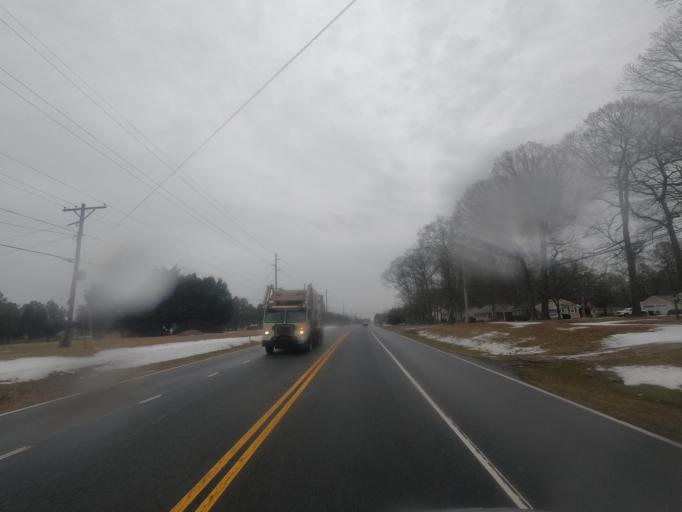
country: US
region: Maryland
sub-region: Dorchester County
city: Cambridge
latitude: 38.5701
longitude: -75.9859
